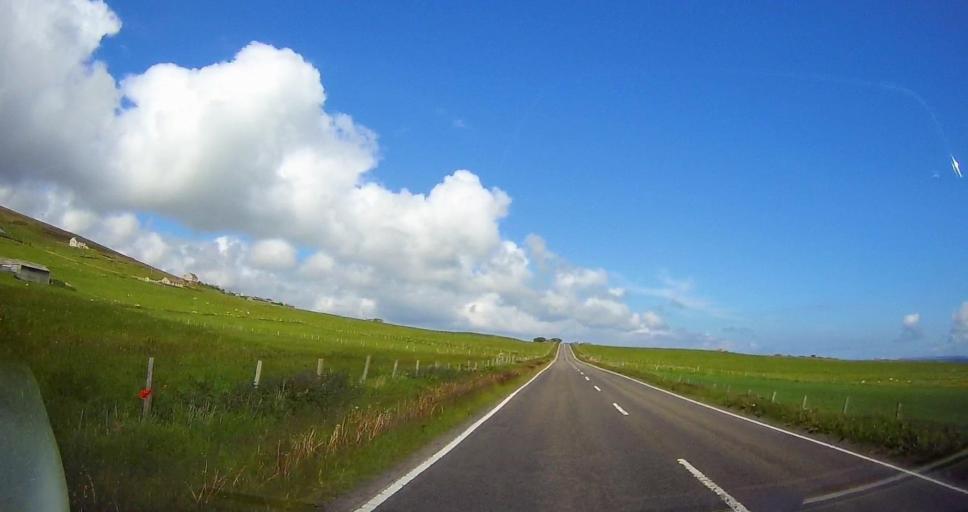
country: GB
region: Scotland
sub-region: Orkney Islands
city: Orkney
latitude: 59.0157
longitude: -3.1066
